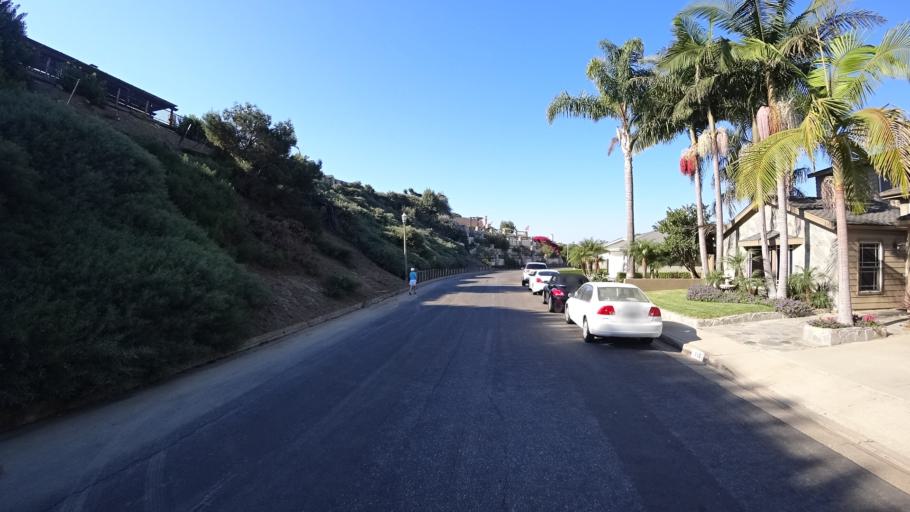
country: US
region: California
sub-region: Orange County
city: San Clemente
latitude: 33.4357
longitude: -117.6079
